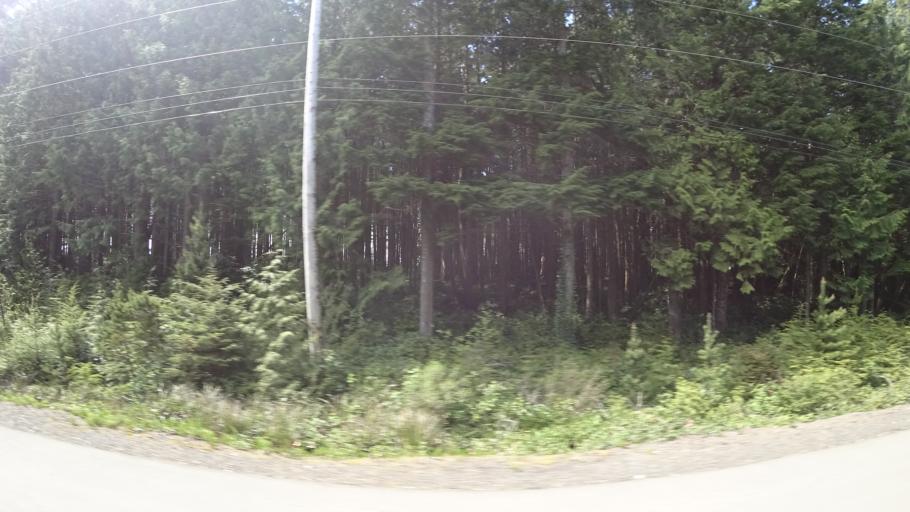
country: US
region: Oregon
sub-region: Lincoln County
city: Lincoln Beach
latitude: 44.8321
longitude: -124.0561
